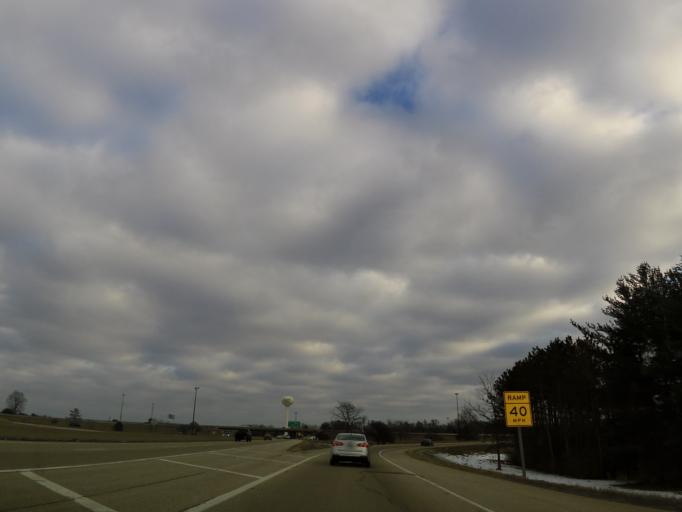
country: US
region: Illinois
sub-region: Winnebago County
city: Cherry Valley
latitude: 42.2401
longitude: -88.9702
